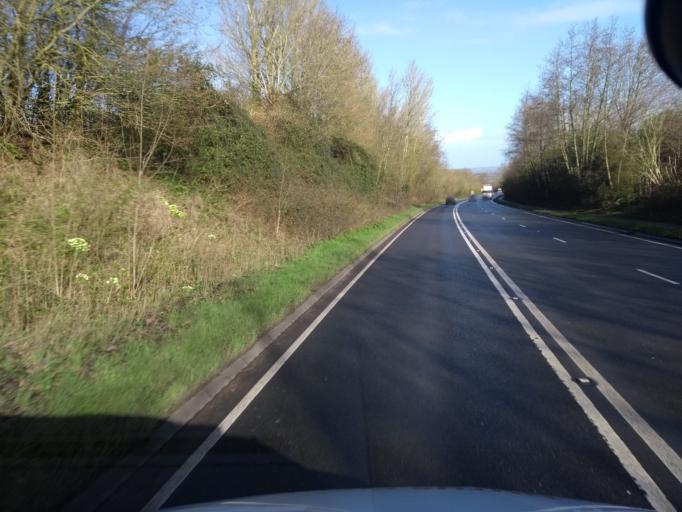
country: GB
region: England
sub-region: Somerset
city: Yeovil
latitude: 50.9601
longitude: -2.6517
